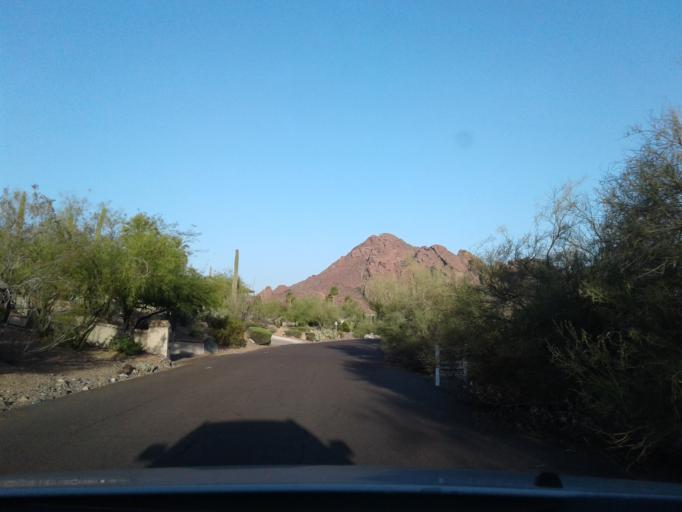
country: US
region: Arizona
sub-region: Maricopa County
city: Paradise Valley
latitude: 33.5269
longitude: -111.9891
